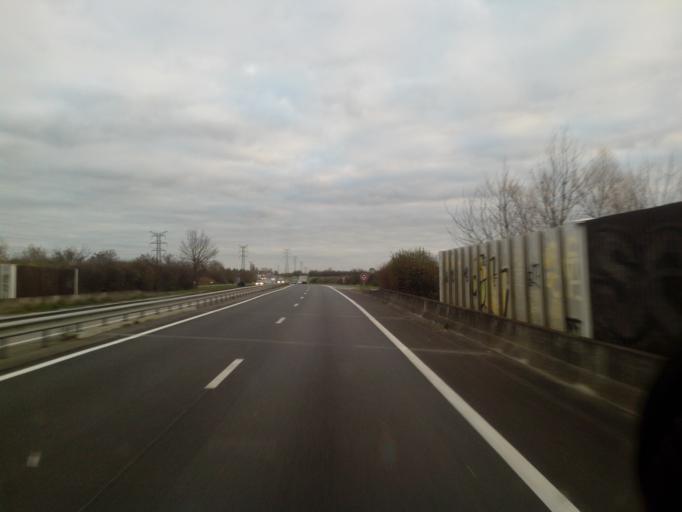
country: FR
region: Poitou-Charentes
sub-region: Departement de la Vienne
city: Mignaloux-Beauvoir
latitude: 46.5847
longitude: 0.3930
